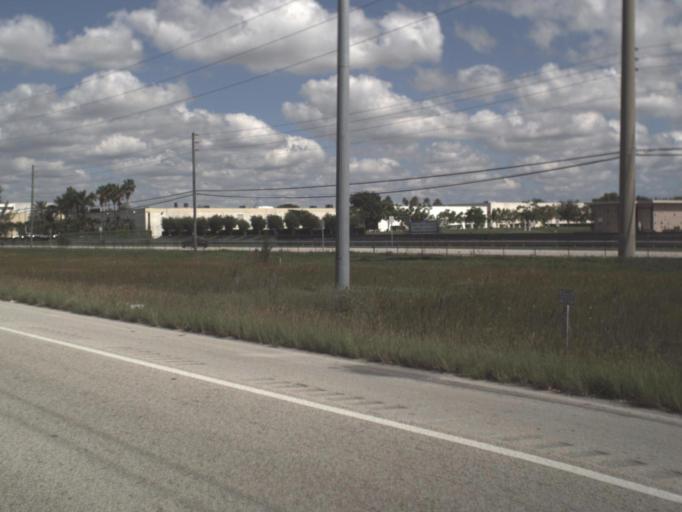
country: US
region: Florida
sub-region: Miami-Dade County
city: Doral
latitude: 25.8023
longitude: -80.3860
